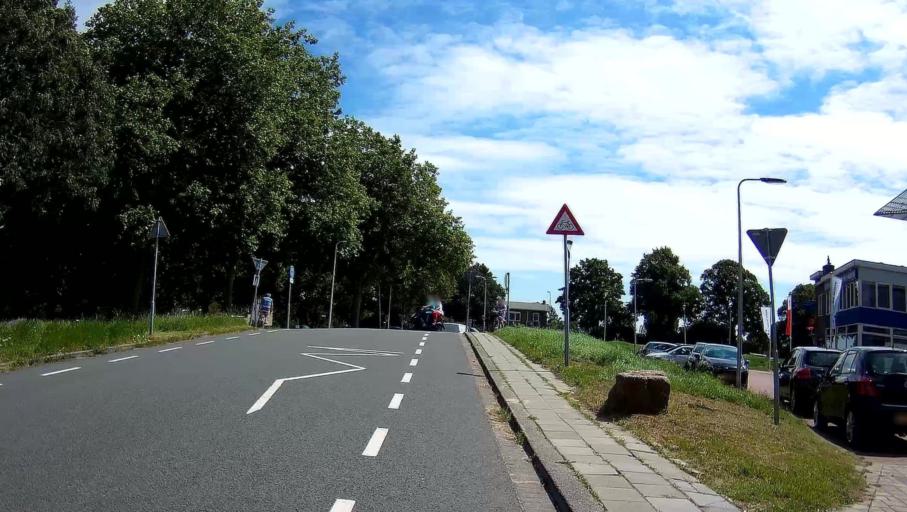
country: NL
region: South Holland
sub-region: Gemeente Capelle aan den IJssel
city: Capelle-West
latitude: 51.9106
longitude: 4.5841
